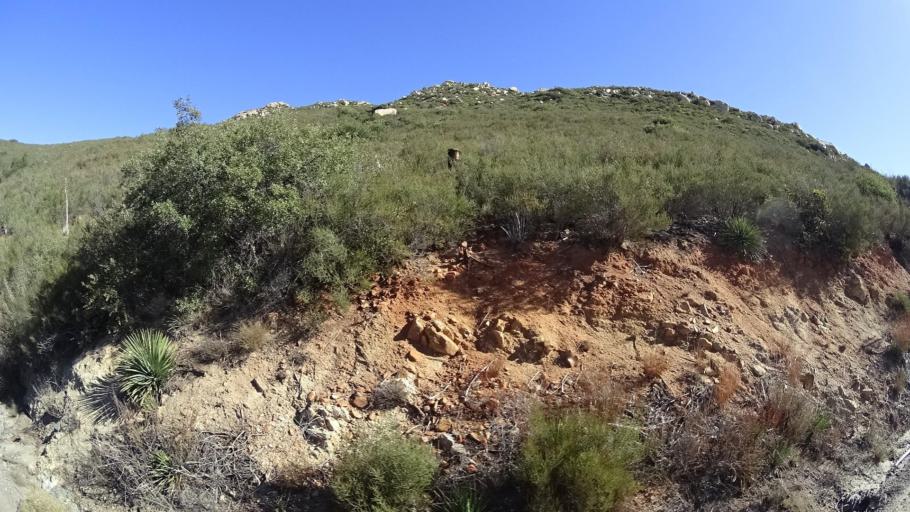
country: US
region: California
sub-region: San Diego County
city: Descanso
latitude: 32.8679
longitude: -116.6543
